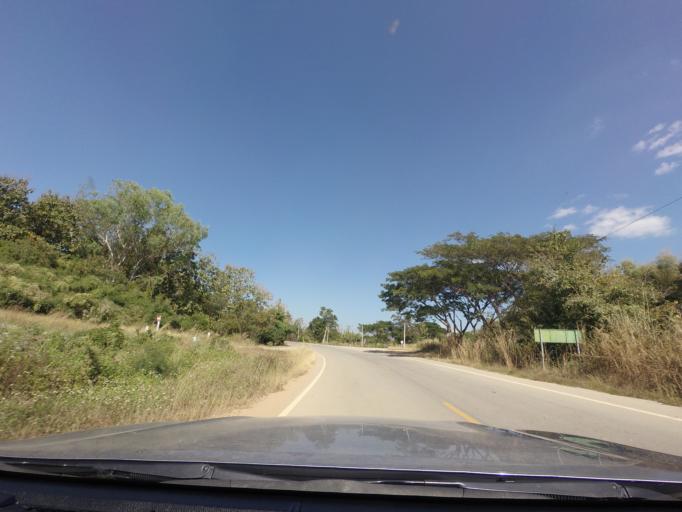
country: TH
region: Lampang
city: Chae Hom
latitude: 18.7020
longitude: 99.5898
